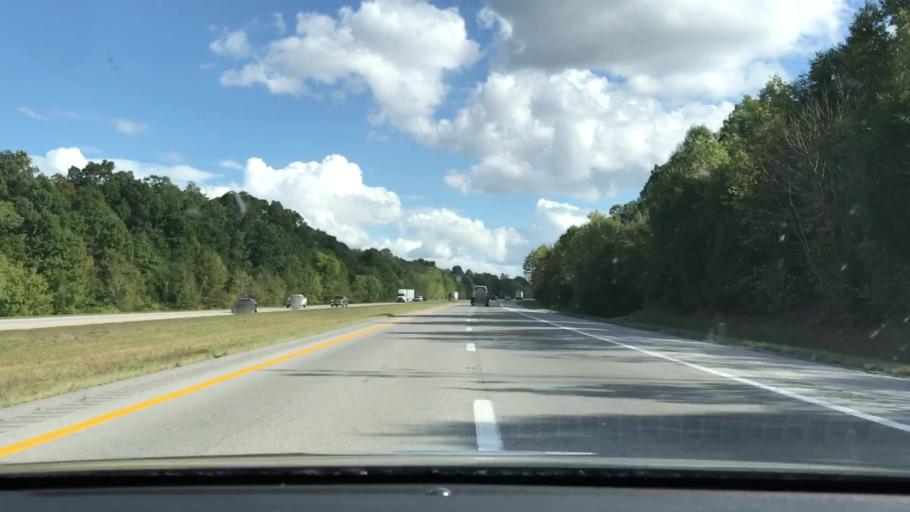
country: US
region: Kentucky
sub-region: Lyon County
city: Eddyville
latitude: 37.0233
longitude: -87.9902
